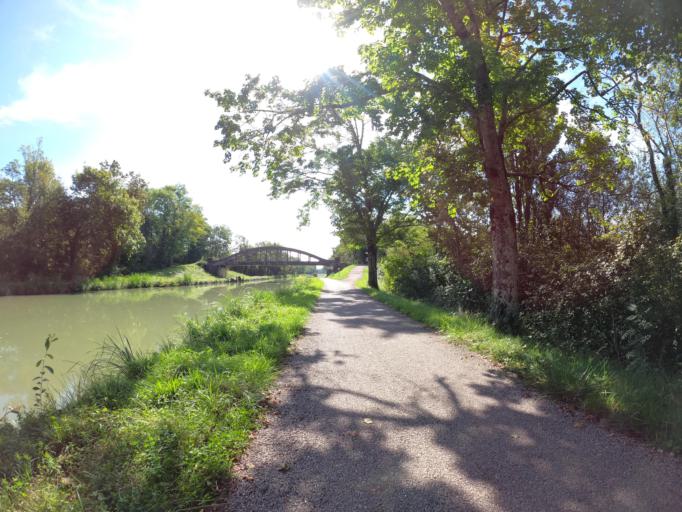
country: FR
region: Midi-Pyrenees
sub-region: Departement du Tarn-et-Garonne
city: Montech
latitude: 43.9348
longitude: 1.2541
